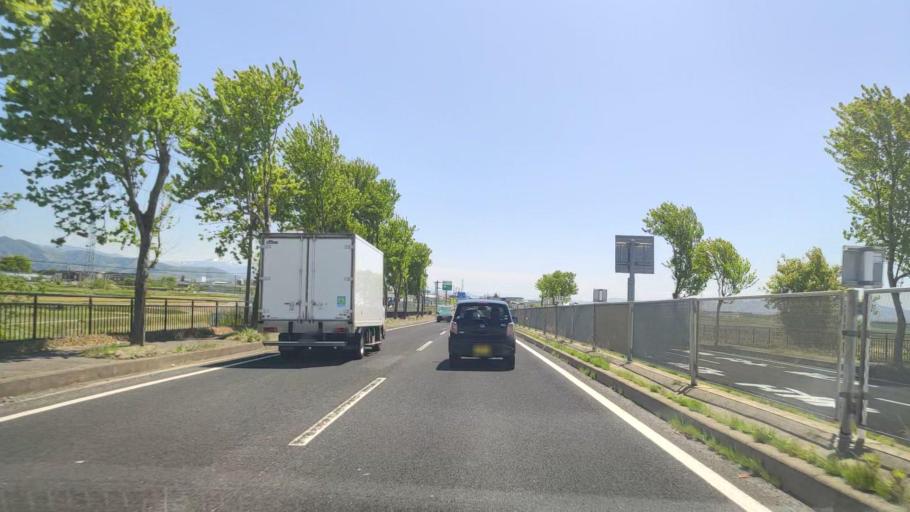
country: JP
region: Yamagata
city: Higashine
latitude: 38.4453
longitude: 140.3811
